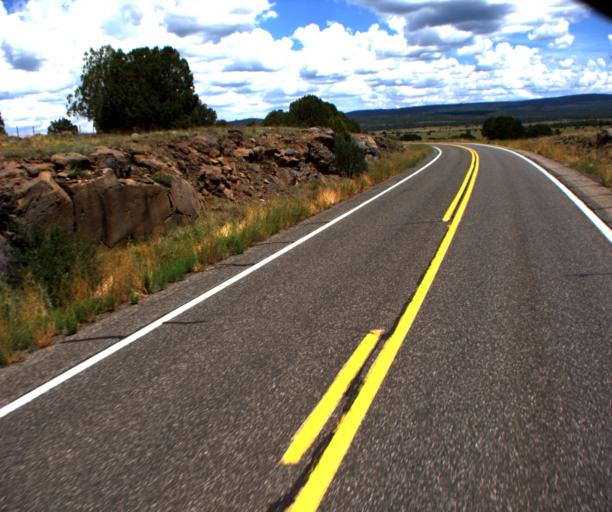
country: US
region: Arizona
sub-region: Gila County
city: Pine
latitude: 34.4876
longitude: -111.6020
